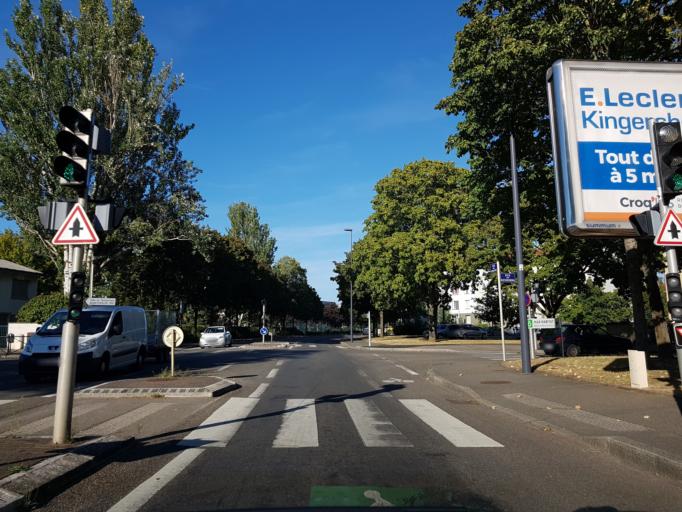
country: FR
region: Alsace
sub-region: Departement du Haut-Rhin
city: Kingersheim
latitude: 47.7752
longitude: 7.3255
